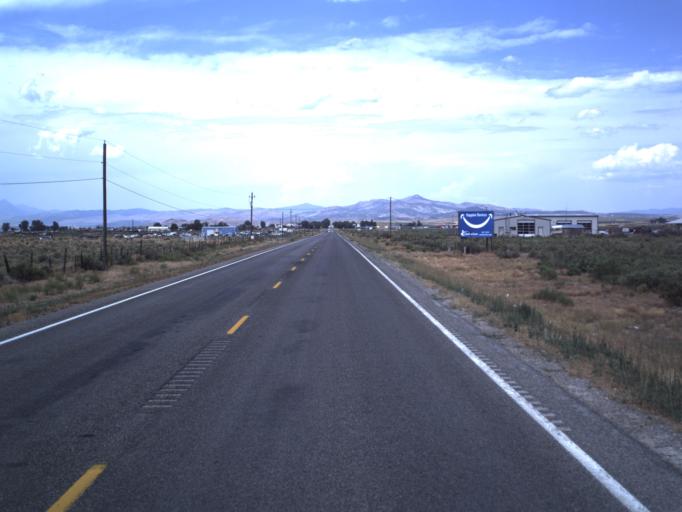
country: US
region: Utah
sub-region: Sanpete County
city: Moroni
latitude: 39.4498
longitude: -111.5625
